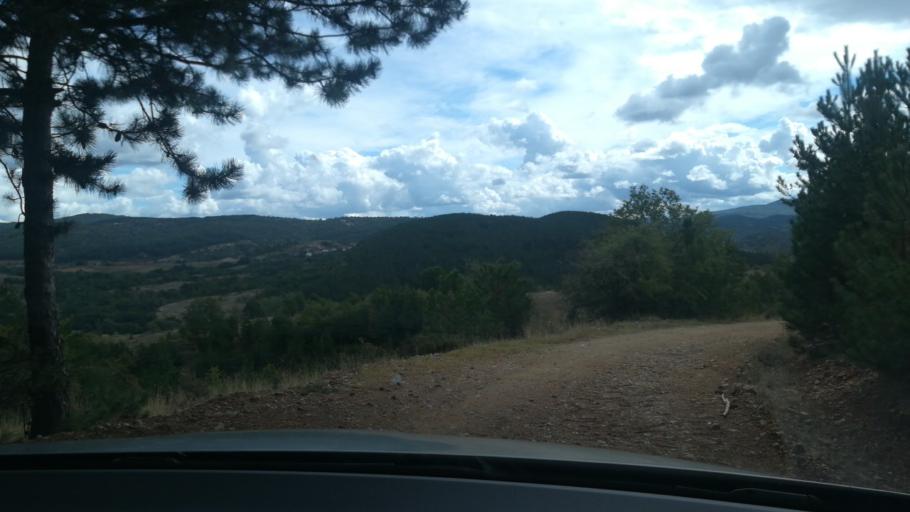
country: MK
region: Makedonska Kamenica
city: Makedonska Kamenica
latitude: 42.0071
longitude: 22.6051
